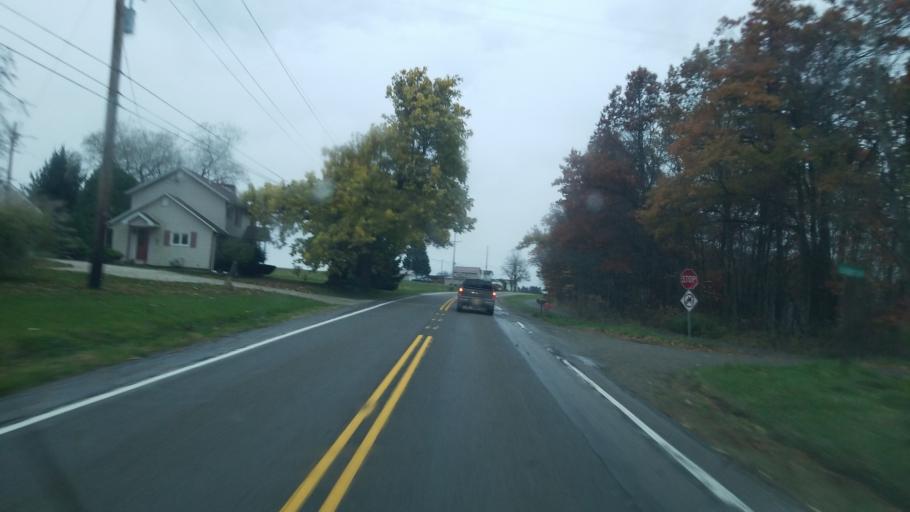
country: US
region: Pennsylvania
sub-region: Clarion County
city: Marianne
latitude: 41.2730
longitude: -79.3909
